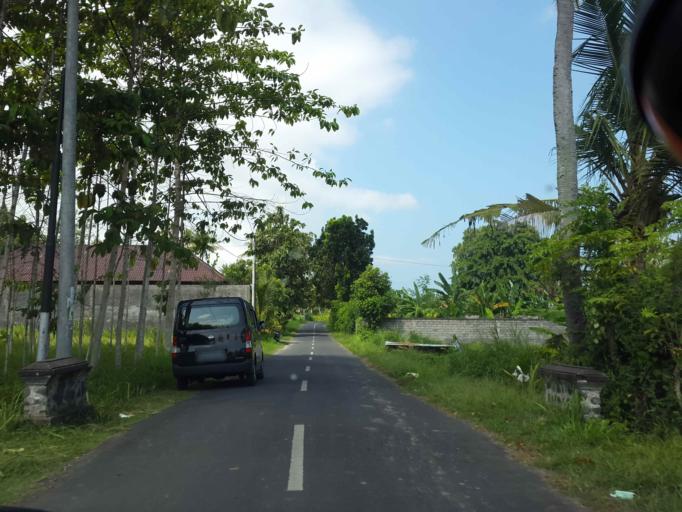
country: ID
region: Bali
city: Klungkung
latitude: -8.5441
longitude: 115.3747
